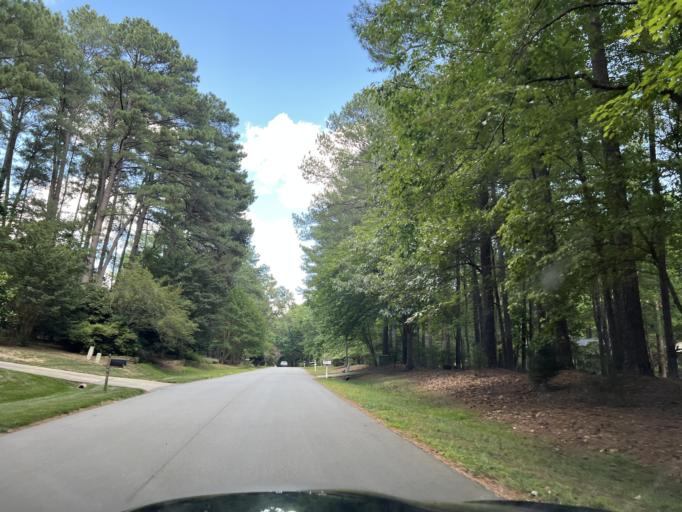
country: US
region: North Carolina
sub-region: Wake County
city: Wake Forest
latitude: 35.9389
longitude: -78.6423
